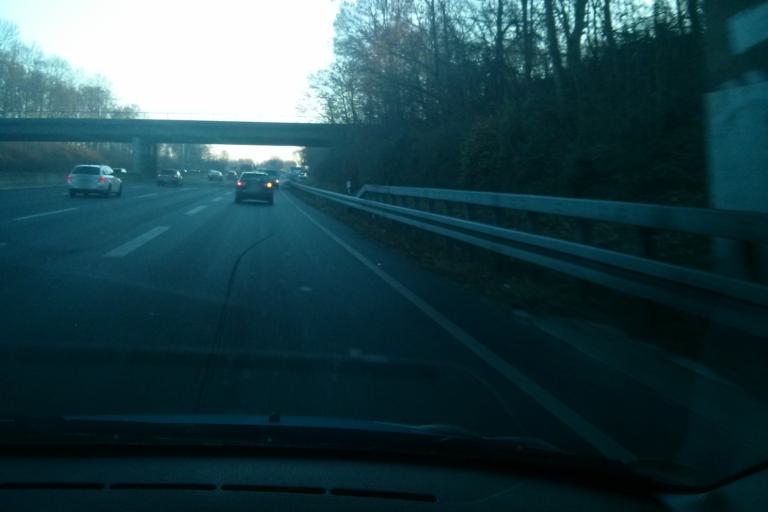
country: DE
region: North Rhine-Westphalia
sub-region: Regierungsbezirk Koln
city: Bonn
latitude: 50.7530
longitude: 7.1411
